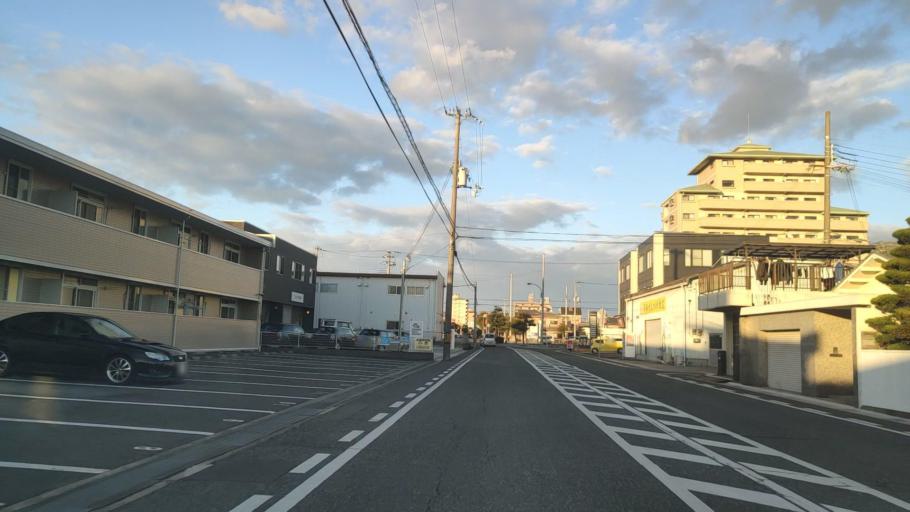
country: JP
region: Hyogo
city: Himeji
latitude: 34.8133
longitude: 134.6889
